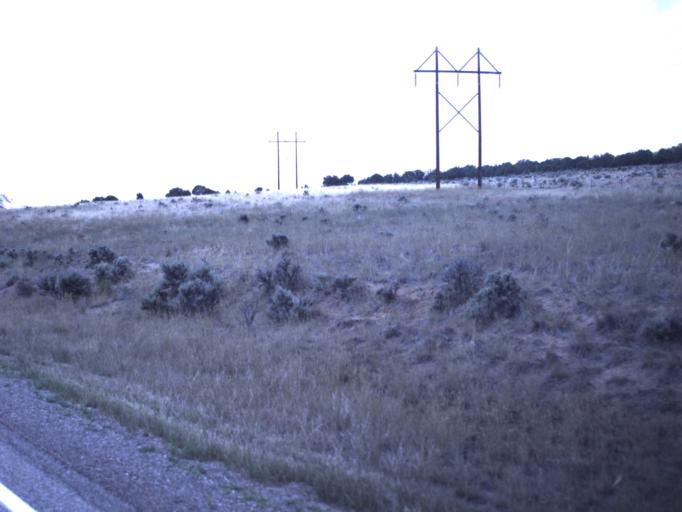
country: US
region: Utah
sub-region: Uintah County
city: Vernal
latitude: 40.5752
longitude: -109.4795
